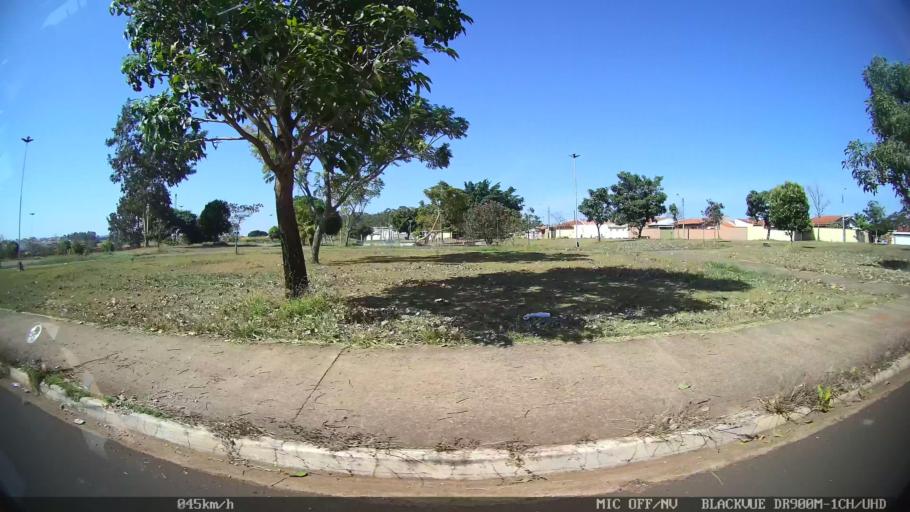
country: BR
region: Sao Paulo
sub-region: Batatais
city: Batatais
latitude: -20.8755
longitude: -47.5940
